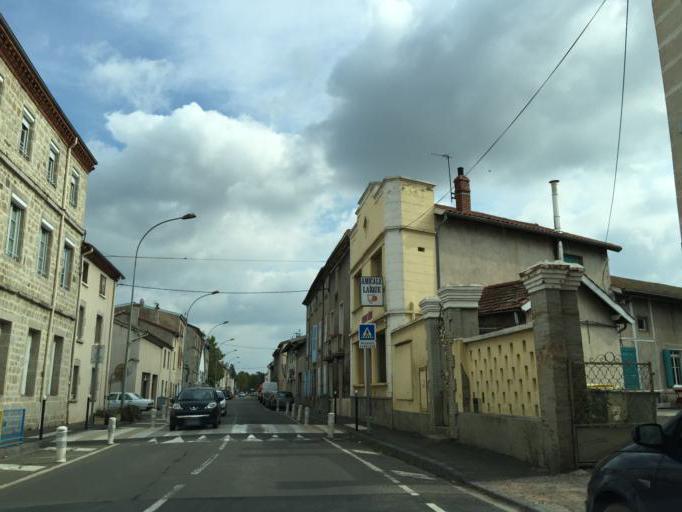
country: FR
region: Rhone-Alpes
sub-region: Departement de la Loire
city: Sury-le-Comtal
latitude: 45.5388
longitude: 4.1858
